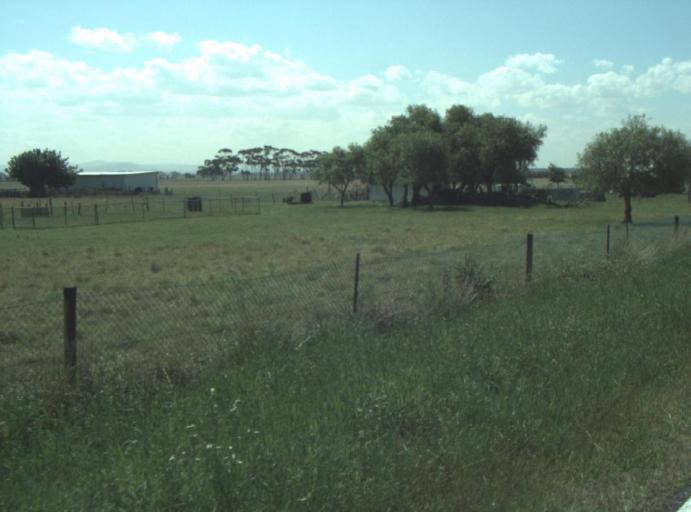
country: AU
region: Victoria
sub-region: Greater Geelong
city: Lara
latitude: -37.9979
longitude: 144.4008
